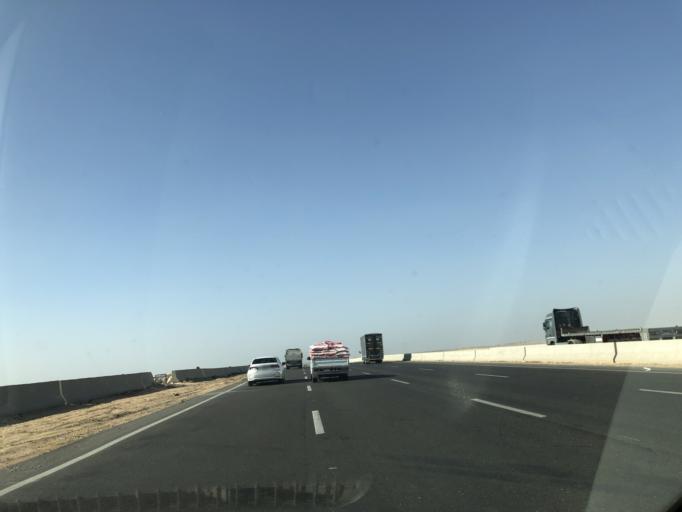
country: EG
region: Muhafazat al Minufiyah
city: Ashmun
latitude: 30.0364
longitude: 30.8459
